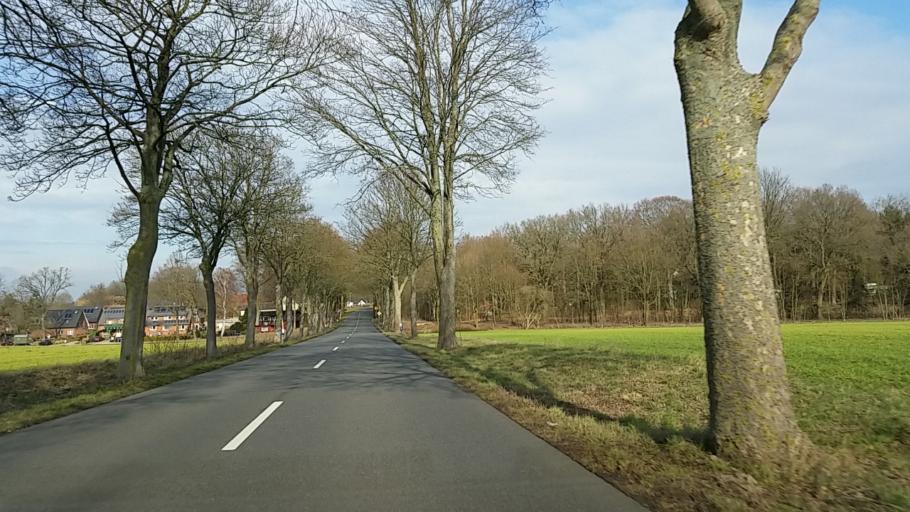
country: DE
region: Lower Saxony
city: Altenmedingen
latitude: 53.1660
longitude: 10.6180
